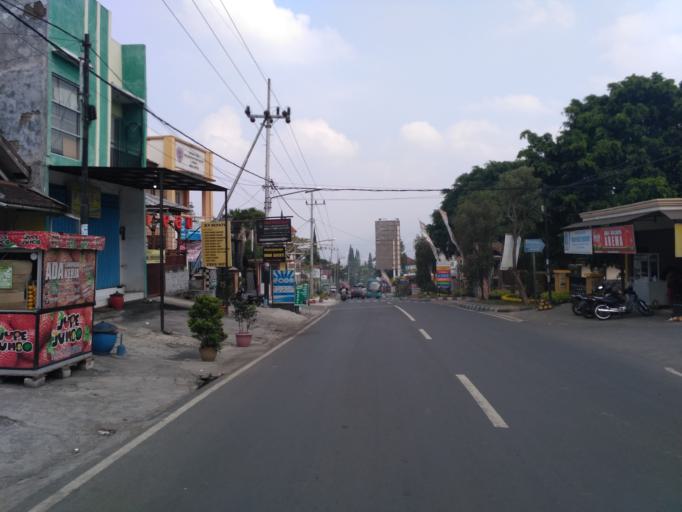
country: ID
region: East Java
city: Batu
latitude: -7.8377
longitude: 112.5283
